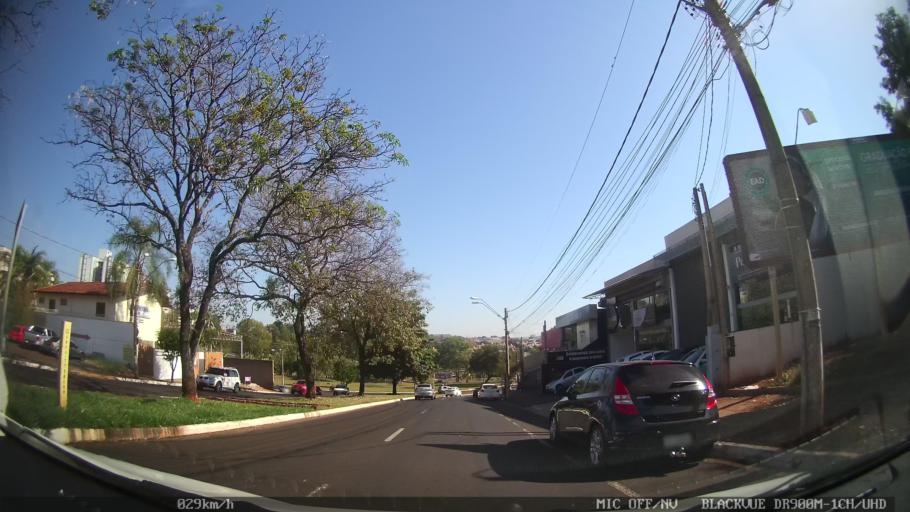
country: BR
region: Sao Paulo
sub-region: Ribeirao Preto
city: Ribeirao Preto
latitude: -21.1956
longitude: -47.8213
